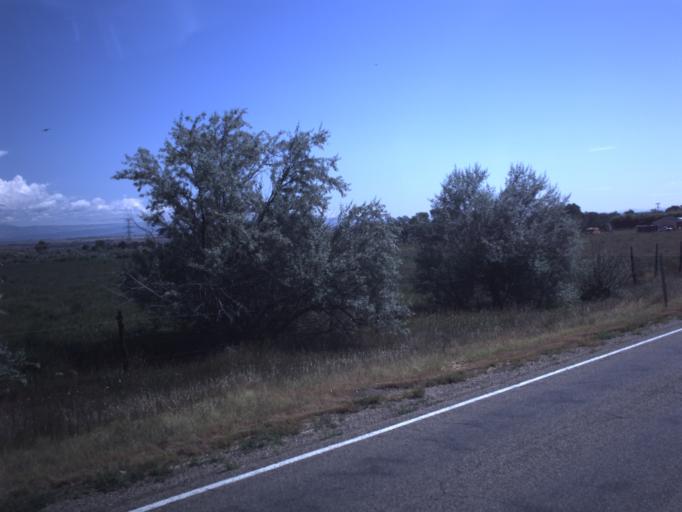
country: US
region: Utah
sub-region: Duchesne County
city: Roosevelt
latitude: 40.2585
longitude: -110.0806
